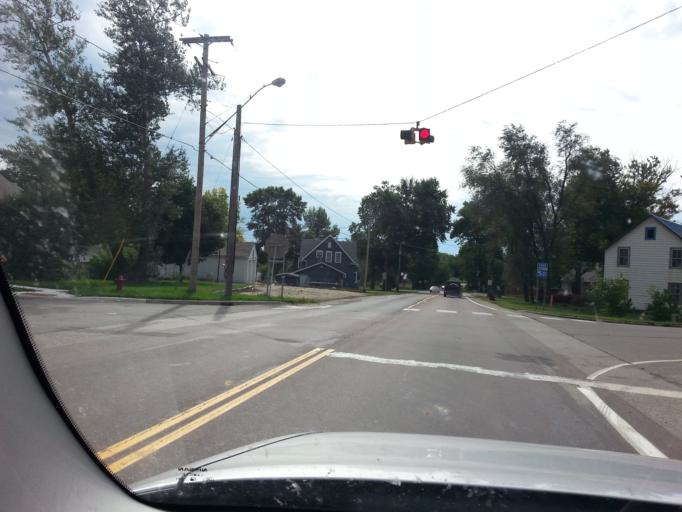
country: US
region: Minnesota
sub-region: Goodhue County
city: Cannon Falls
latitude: 44.6106
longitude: -93.0022
